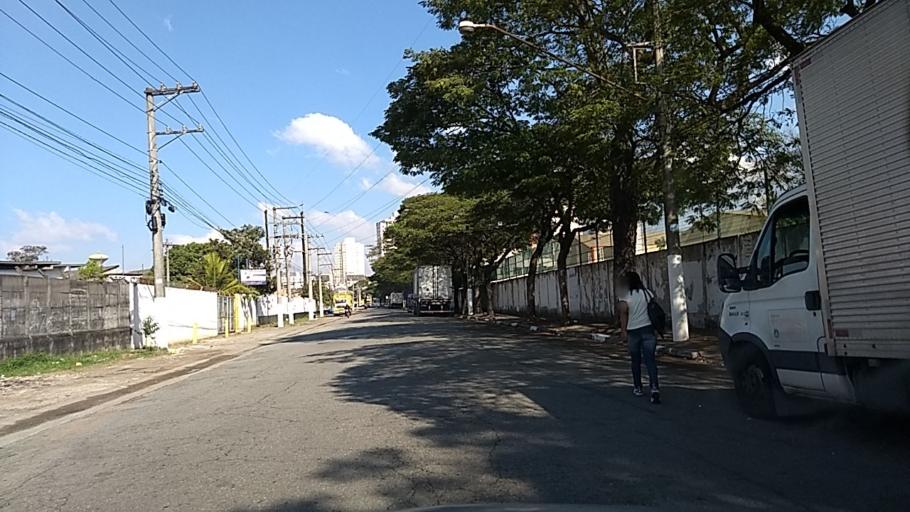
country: BR
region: Sao Paulo
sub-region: Osasco
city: Osasco
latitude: -23.5259
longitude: -46.7863
